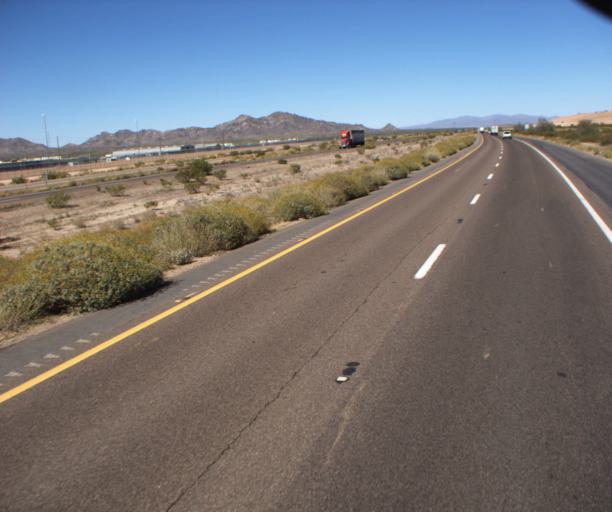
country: US
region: Arizona
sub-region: Maricopa County
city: Buckeye
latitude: 33.2050
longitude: -112.6468
